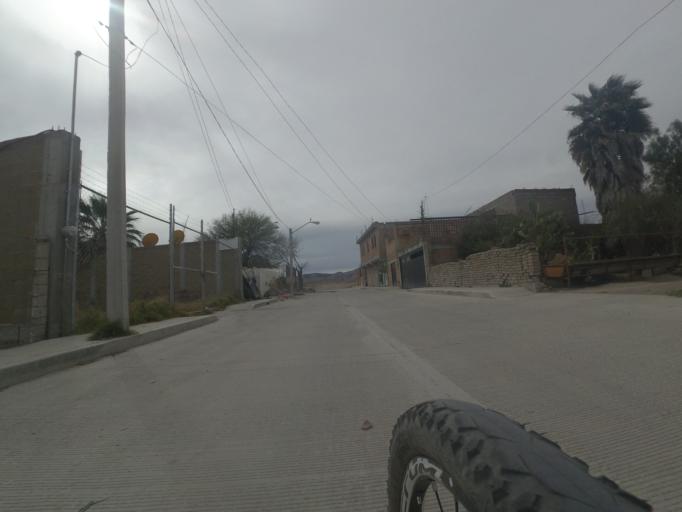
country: MX
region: Aguascalientes
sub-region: Aguascalientes
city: La Loma de los Negritos
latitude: 21.8444
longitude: -102.3563
